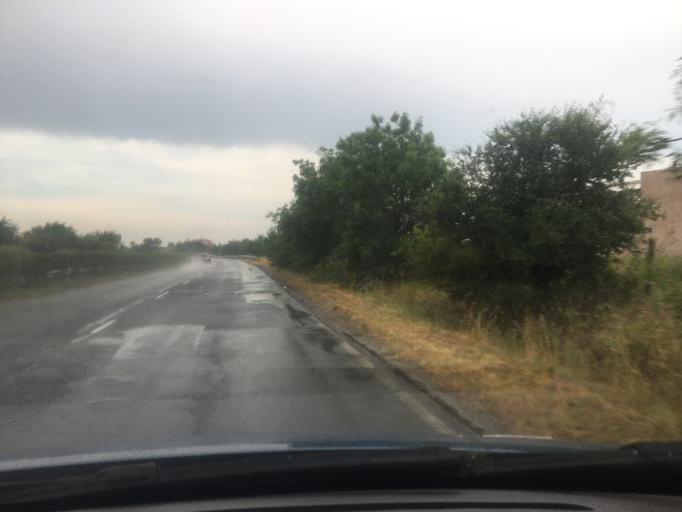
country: BG
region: Burgas
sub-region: Obshtina Burgas
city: Burgas
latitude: 42.5637
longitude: 27.5360
